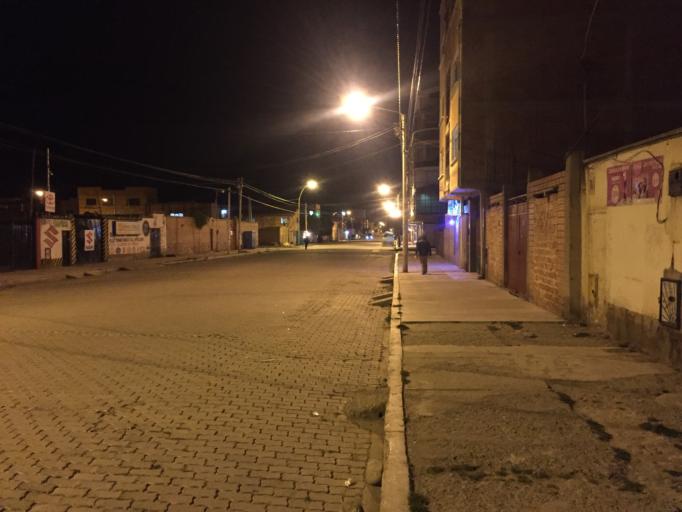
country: BO
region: La Paz
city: La Paz
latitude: -16.5300
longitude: -68.1482
